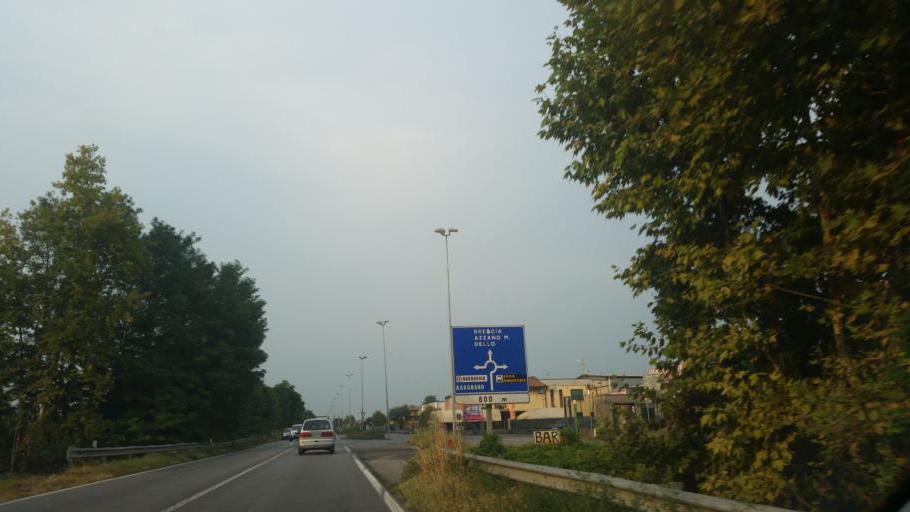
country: IT
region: Lombardy
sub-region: Provincia di Brescia
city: Barbariga
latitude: 45.3934
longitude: 10.0671
